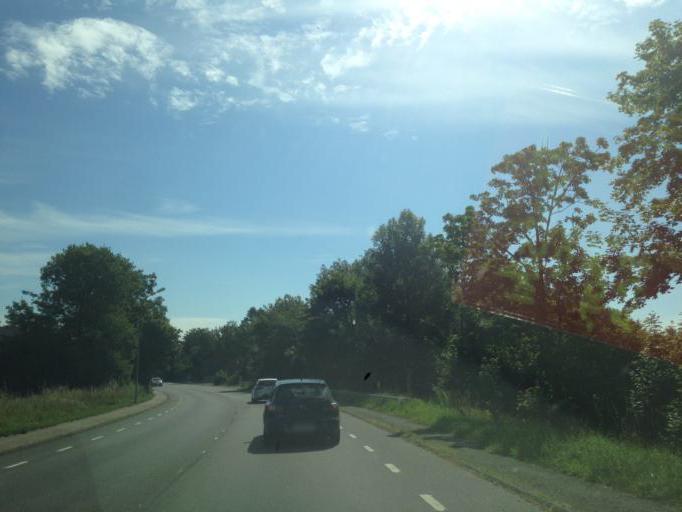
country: SE
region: Skane
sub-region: Simrishamns Kommun
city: Kivik
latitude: 55.6353
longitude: 14.1244
